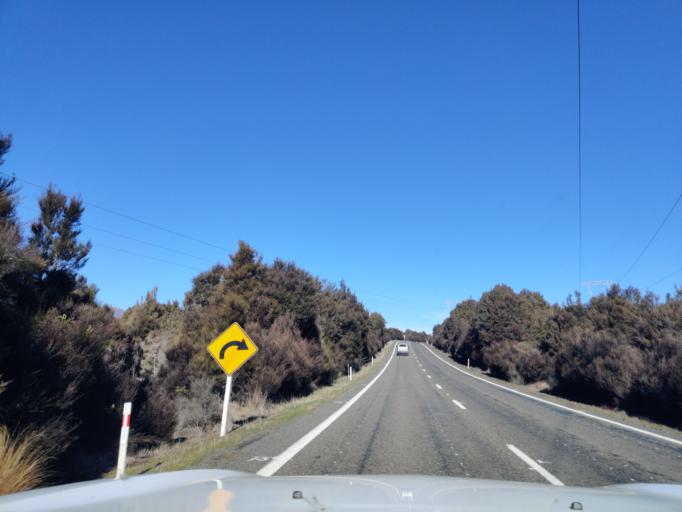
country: NZ
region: Waikato
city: Turangi
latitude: -39.2011
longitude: 175.7566
